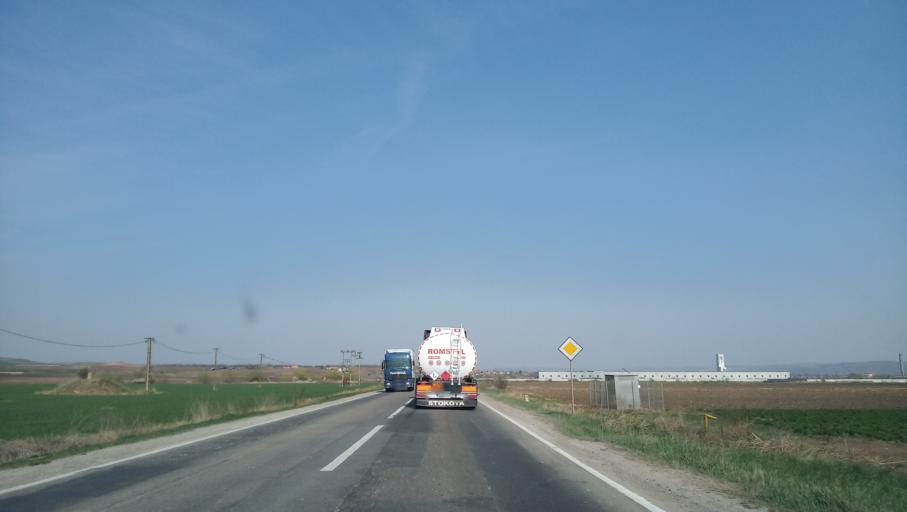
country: RO
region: Alba
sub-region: Oras Teius
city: Teius
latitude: 46.1819
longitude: 23.6577
